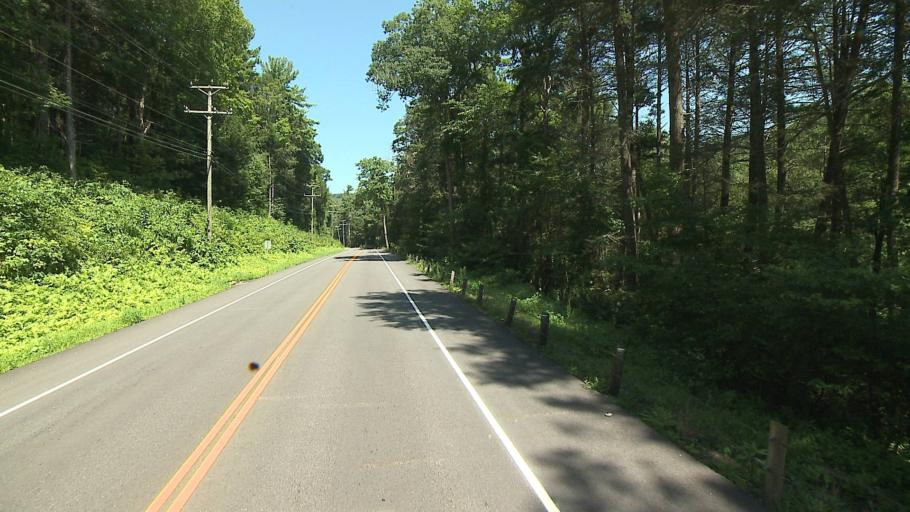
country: US
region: Connecticut
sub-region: Litchfield County
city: New Preston
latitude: 41.8342
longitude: -73.3478
